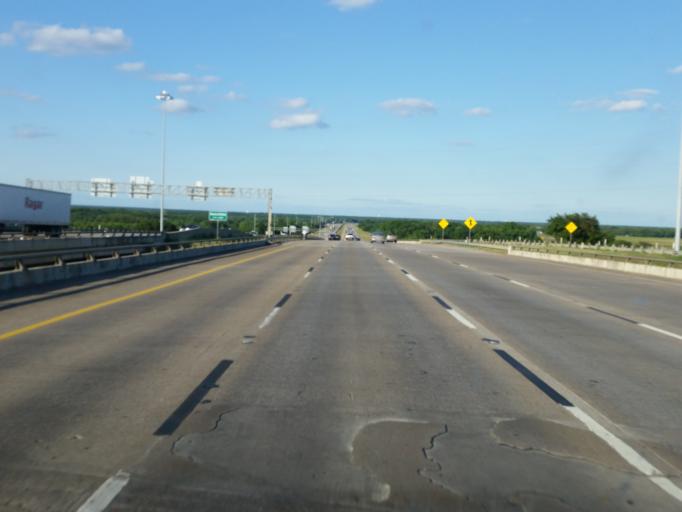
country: US
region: Texas
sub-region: Dallas County
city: Hutchins
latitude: 32.6635
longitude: -96.7228
